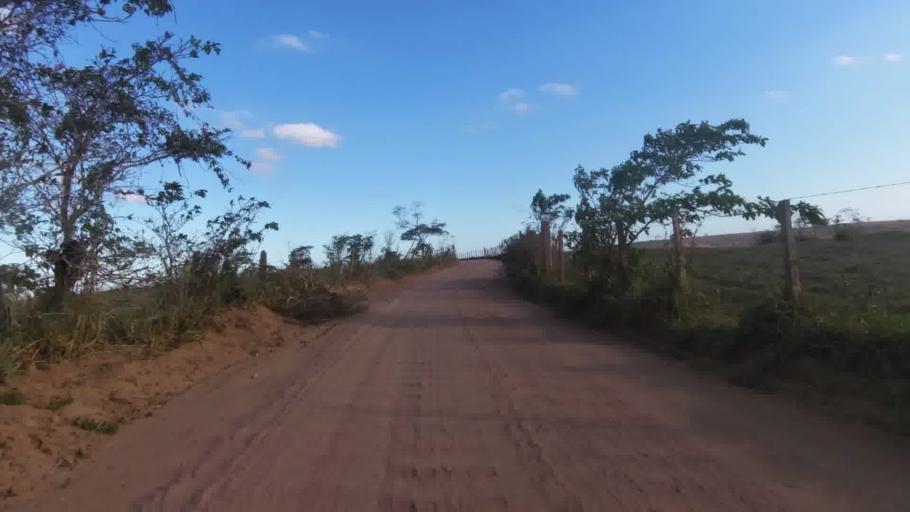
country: BR
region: Espirito Santo
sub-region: Marataizes
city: Marataizes
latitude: -21.1580
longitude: -41.0587
